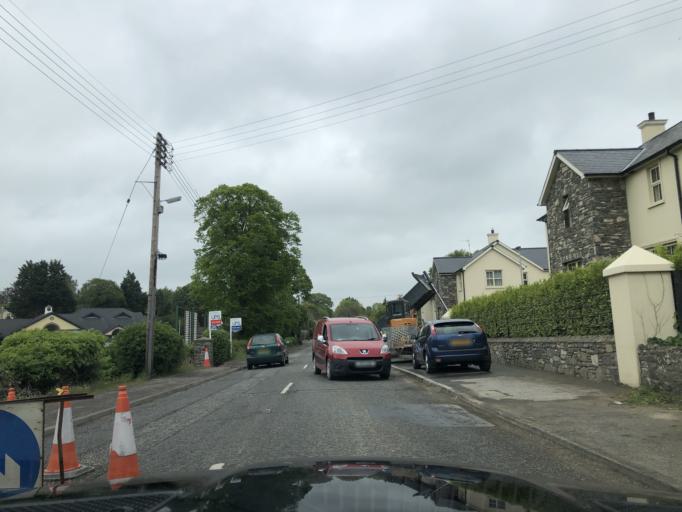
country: GB
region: Northern Ireland
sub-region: Down District
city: Downpatrick
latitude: 54.3367
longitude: -5.7147
